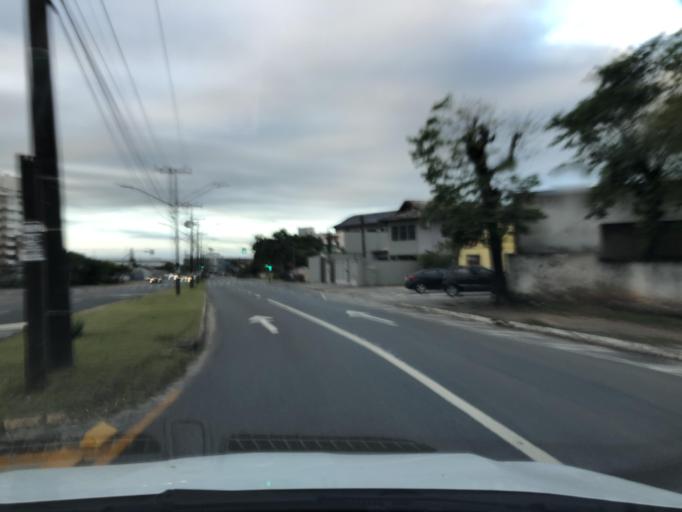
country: BR
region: Santa Catarina
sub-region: Joinville
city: Joinville
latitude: -26.2684
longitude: -48.8624
